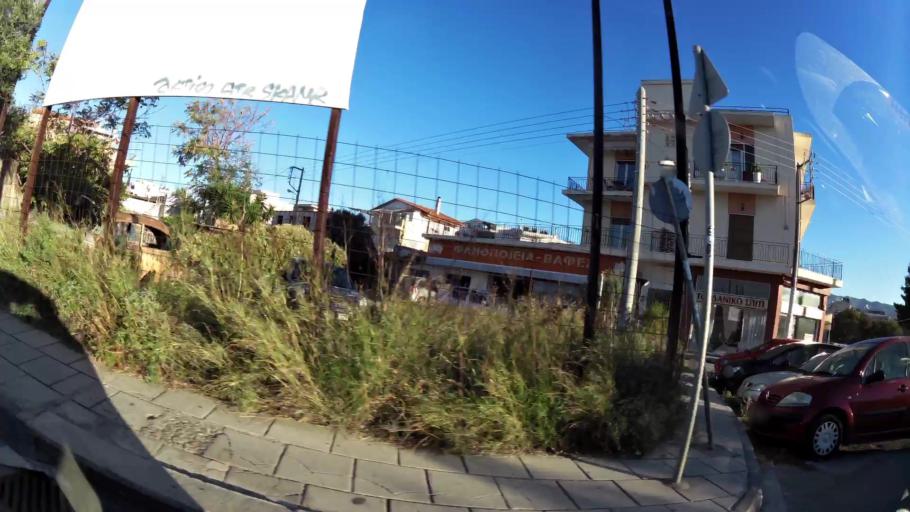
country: GR
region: Attica
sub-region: Nomarchia Athinas
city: Agia Paraskevi
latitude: 38.0221
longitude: 23.8225
